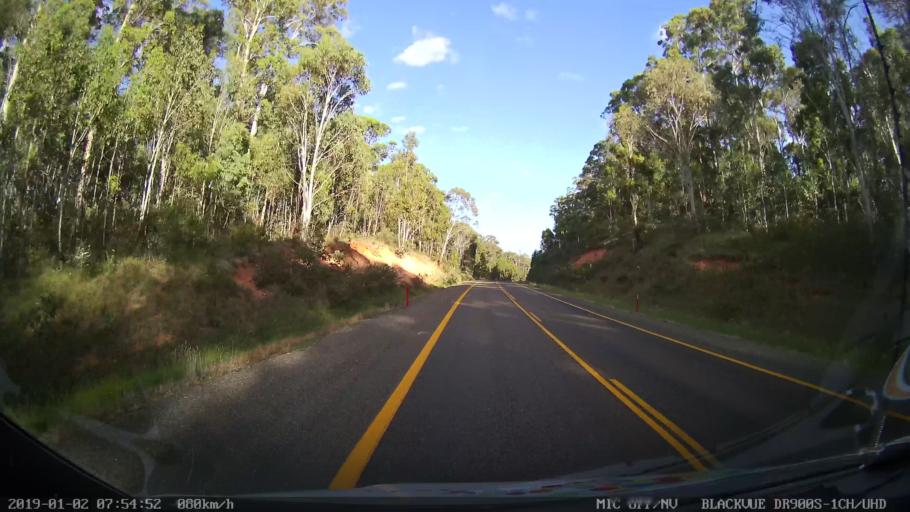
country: AU
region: New South Wales
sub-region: Tumut Shire
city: Tumut
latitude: -35.6912
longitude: 148.4919
